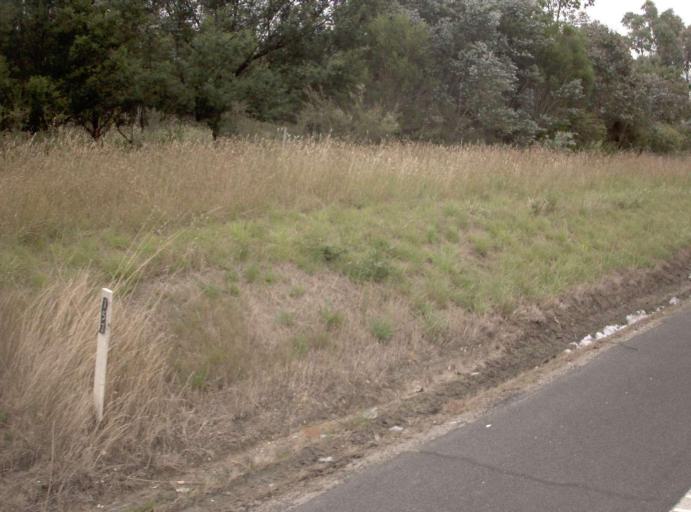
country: AU
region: Victoria
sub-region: Latrobe
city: Traralgon
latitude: -38.2133
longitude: 146.4831
